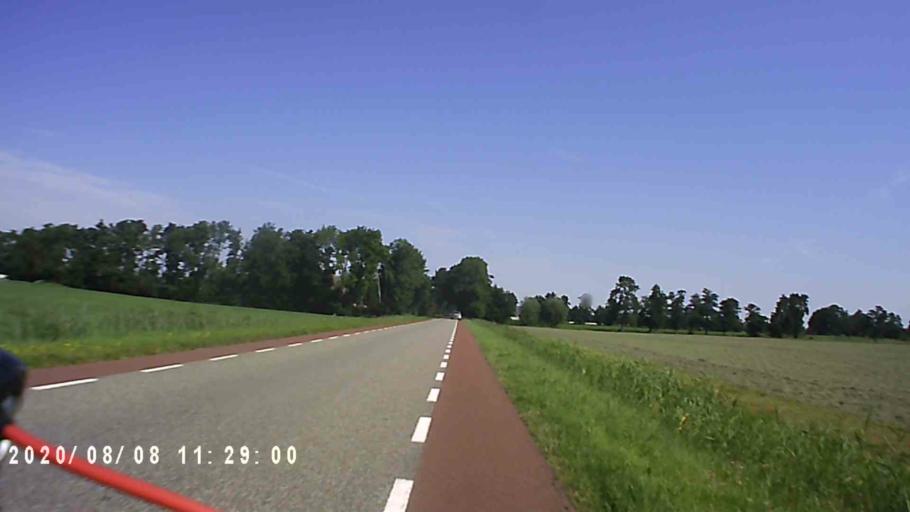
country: NL
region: Groningen
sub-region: Gemeente Leek
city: Leek
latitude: 53.1945
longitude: 6.3865
